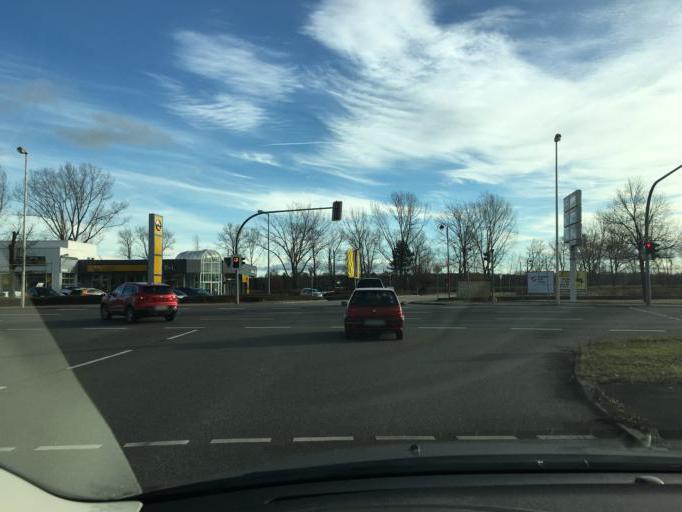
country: DE
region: Saxony
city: Glauchau
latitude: 50.8212
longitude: 12.5162
